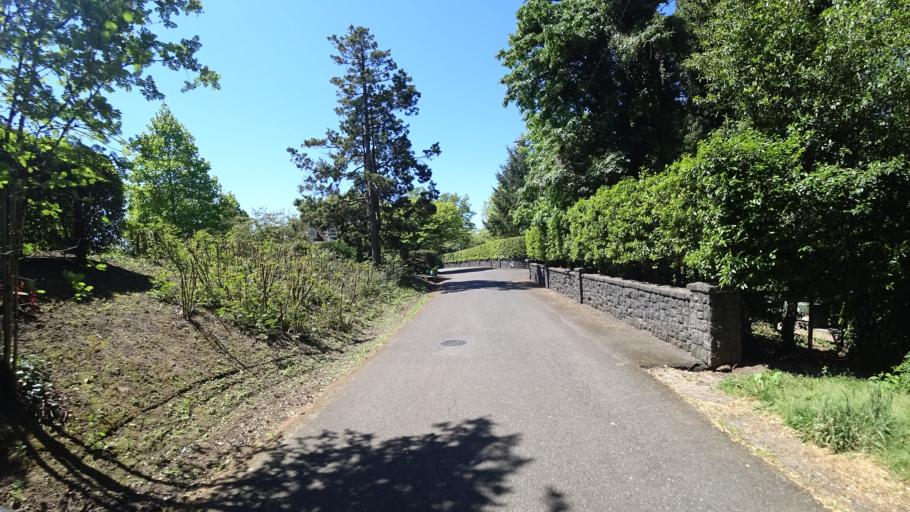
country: US
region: Oregon
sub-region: Washington County
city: West Slope
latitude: 45.5031
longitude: -122.7207
